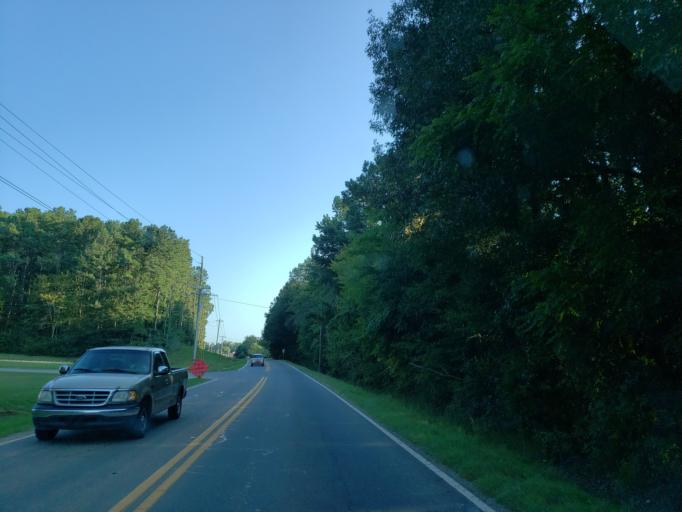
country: US
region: Georgia
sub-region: Murray County
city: Chatsworth
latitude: 34.7344
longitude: -84.8206
